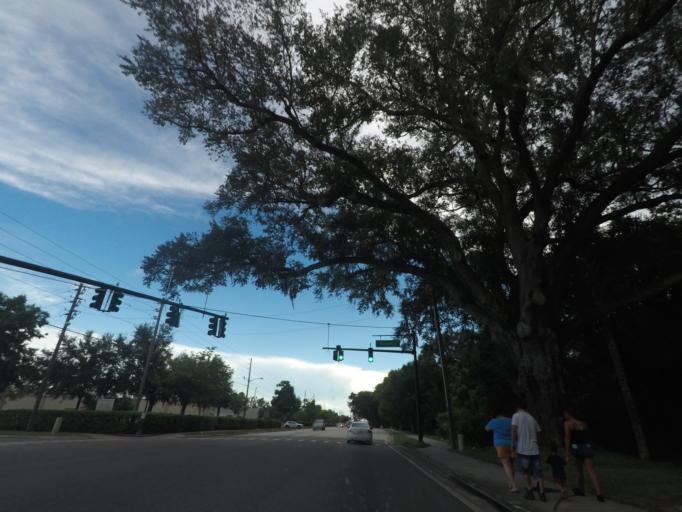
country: US
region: Florida
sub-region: Osceola County
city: Kissimmee
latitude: 28.3084
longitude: -81.4450
